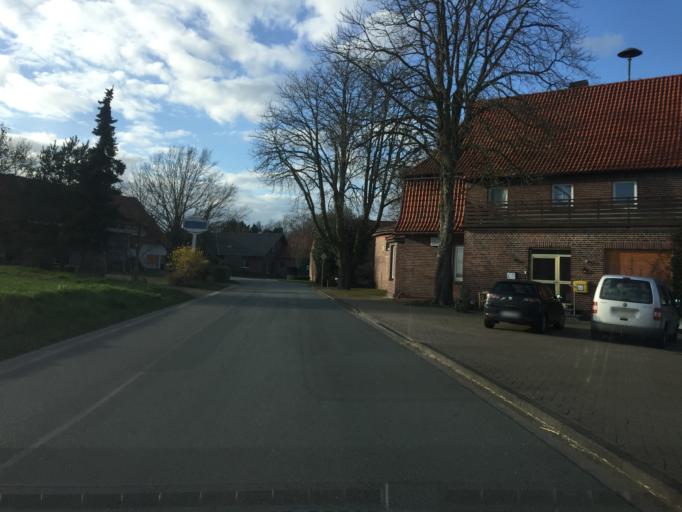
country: DE
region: Lower Saxony
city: Uchte
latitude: 52.5565
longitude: 8.9265
